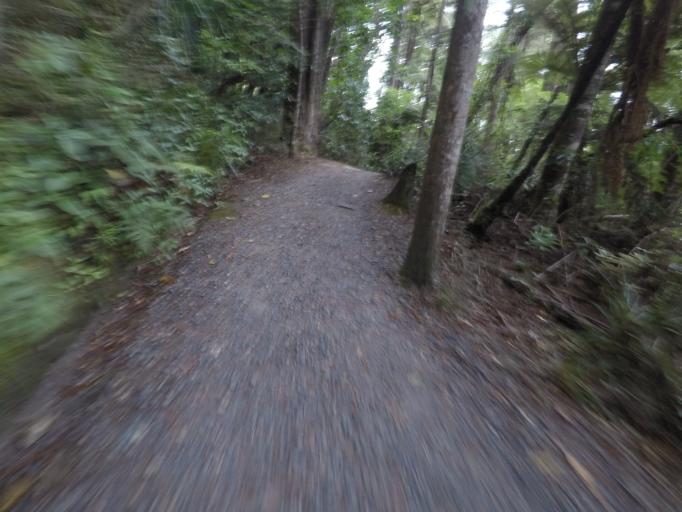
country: NZ
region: Northland
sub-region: Whangarei
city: Whangarei
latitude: -35.7138
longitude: 174.3306
